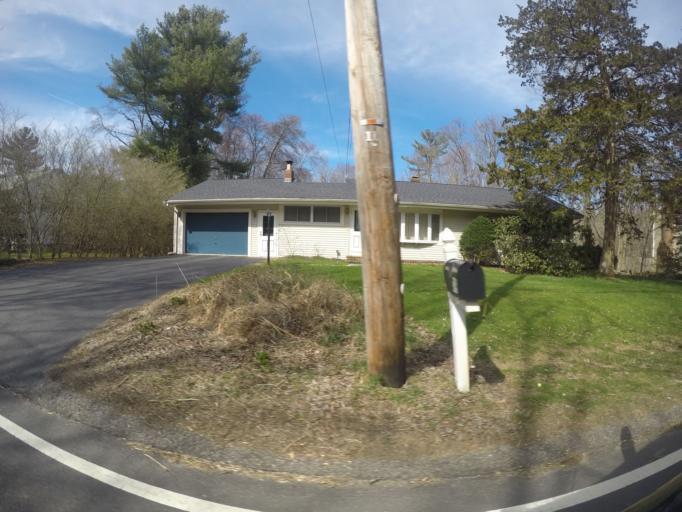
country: US
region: Massachusetts
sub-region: Bristol County
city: Easton
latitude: 42.0439
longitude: -71.0944
